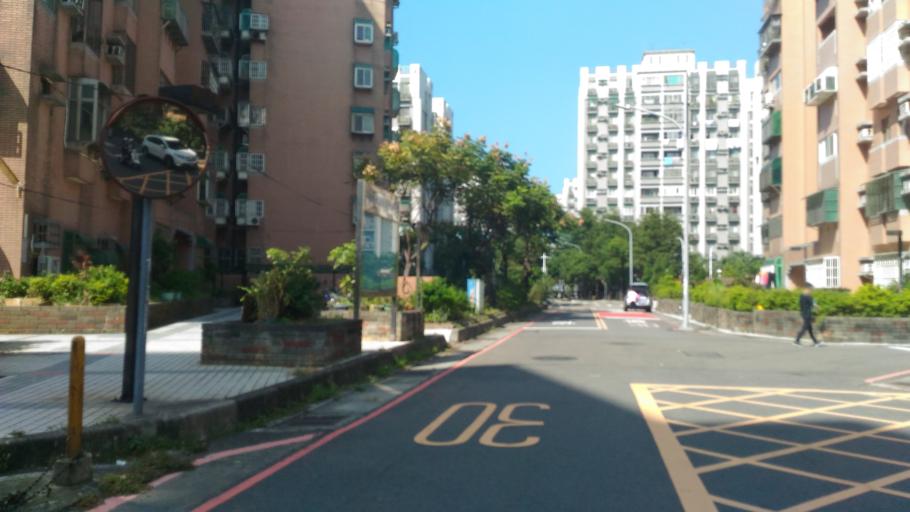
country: TW
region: Taiwan
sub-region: Hsinchu
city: Hsinchu
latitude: 24.8164
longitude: 120.9661
